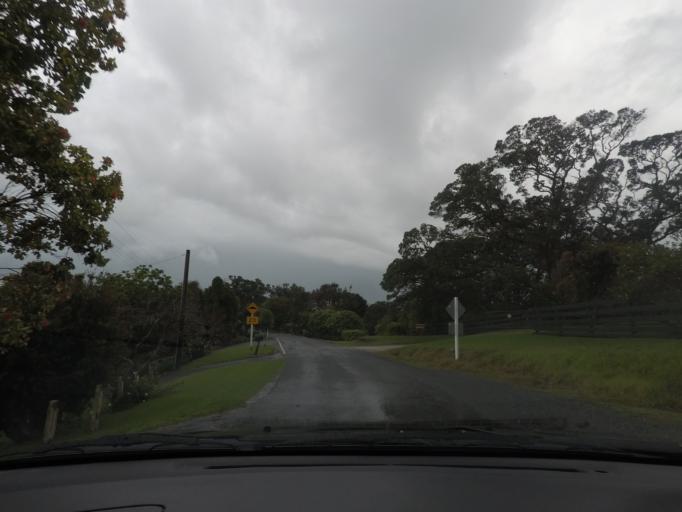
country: NZ
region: Auckland
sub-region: Auckland
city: Warkworth
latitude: -36.4820
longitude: 174.7286
